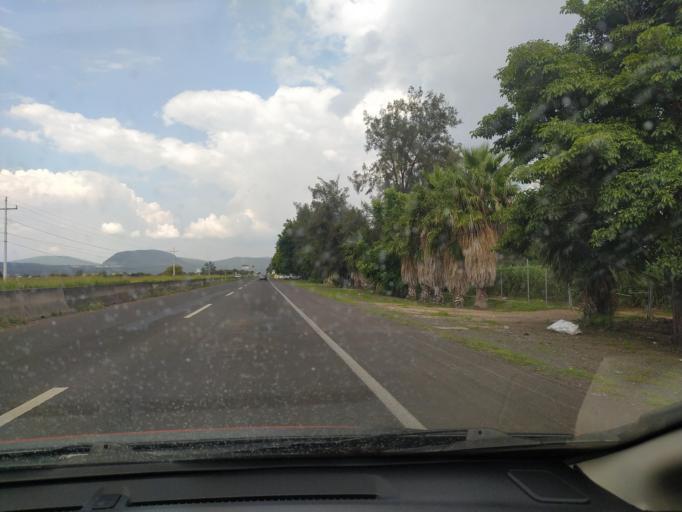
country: MX
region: Jalisco
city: Bellavista
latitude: 20.4133
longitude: -103.6355
